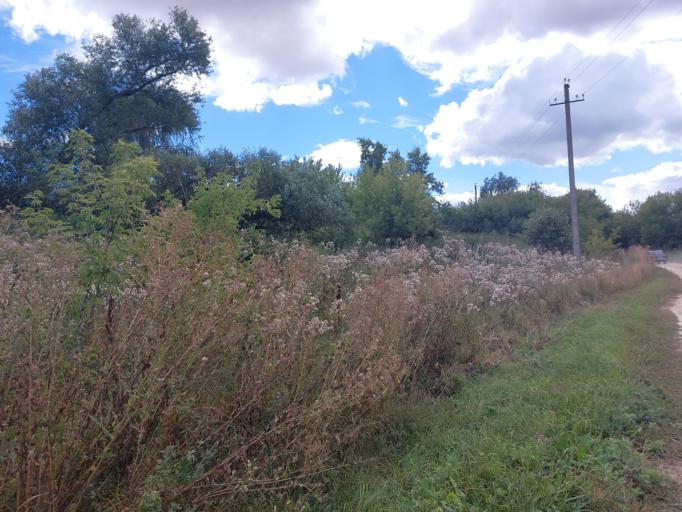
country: RU
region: Lipetsk
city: Terbuny
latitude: 52.2626
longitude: 38.2070
